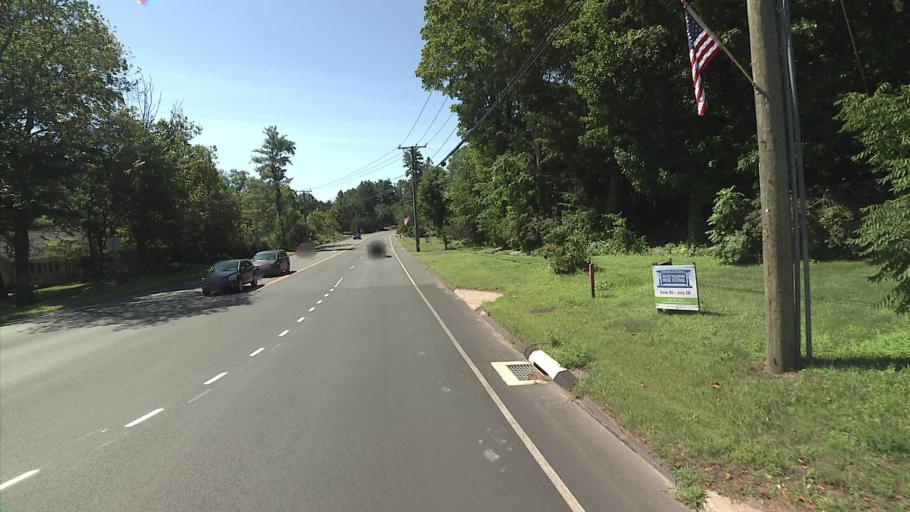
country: US
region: Connecticut
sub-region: Hartford County
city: Weatogue
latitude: 41.8464
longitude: -72.8112
